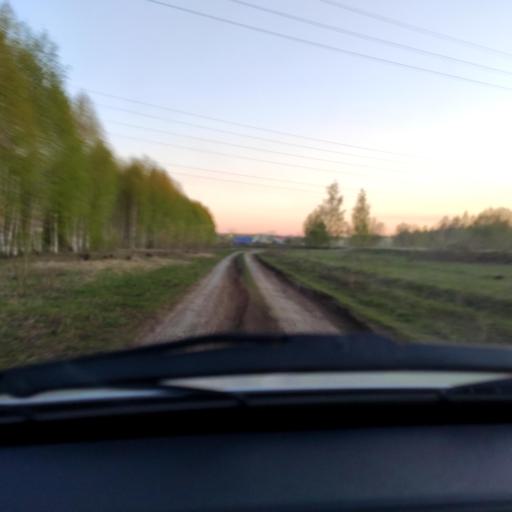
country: RU
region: Bashkortostan
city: Iglino
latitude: 54.7470
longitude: 56.2805
